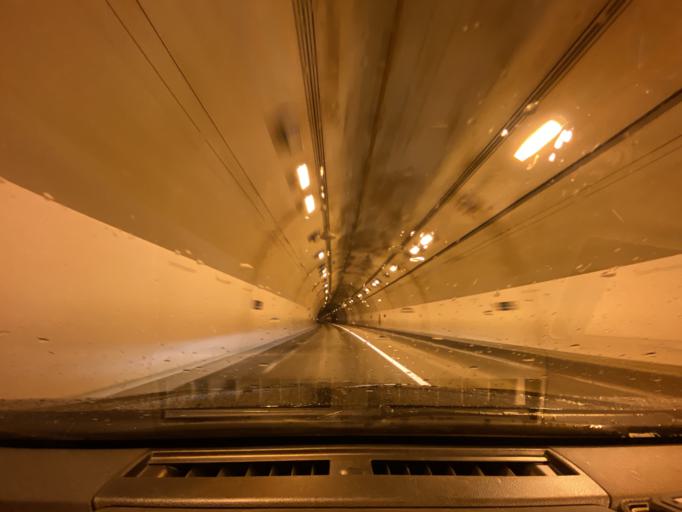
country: JP
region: Hokkaido
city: Rumoi
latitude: 43.6884
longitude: 141.3405
